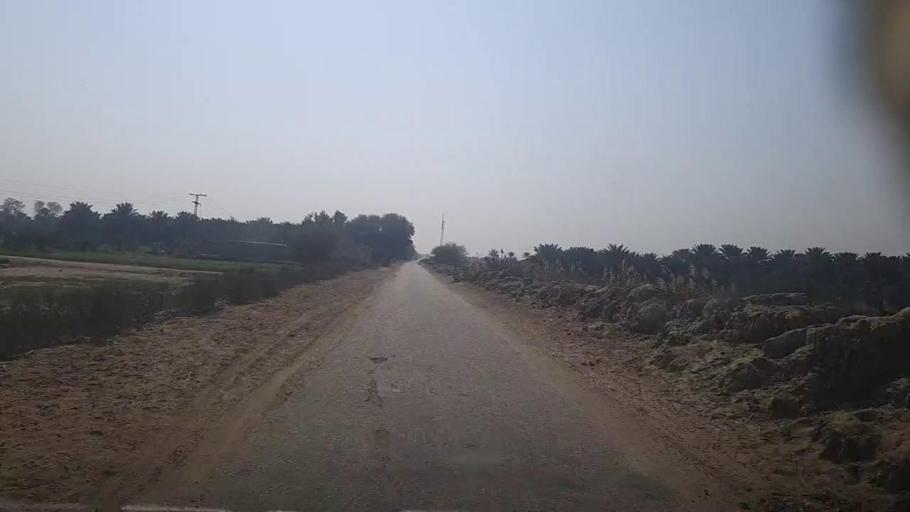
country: PK
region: Sindh
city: Khairpur
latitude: 27.4521
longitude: 68.8125
